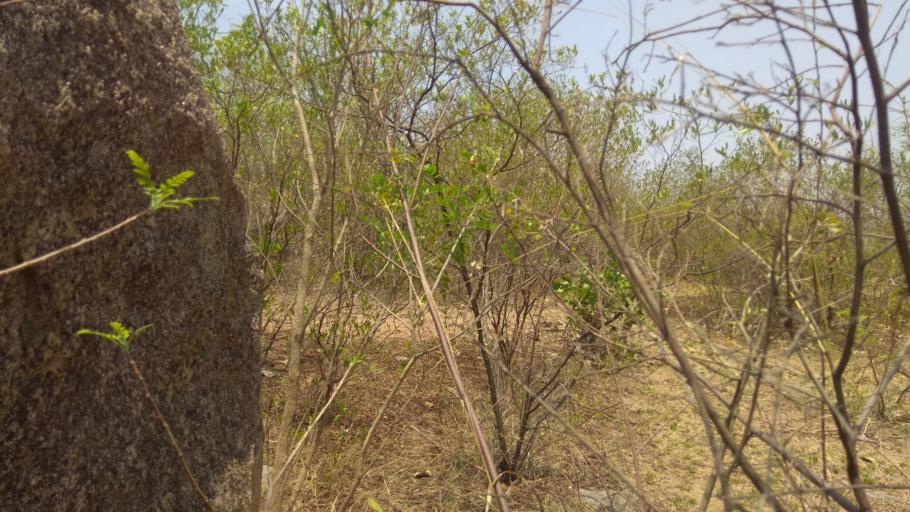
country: IN
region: Telangana
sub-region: Mahbubnagar
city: Farrukhnagar
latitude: 16.8857
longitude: 78.4985
